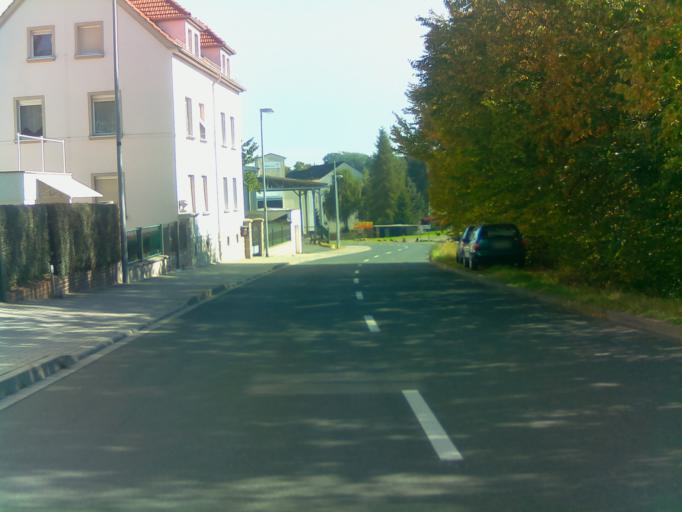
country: DE
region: Thuringia
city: Munchenbernsdorf
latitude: 50.8152
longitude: 11.9210
